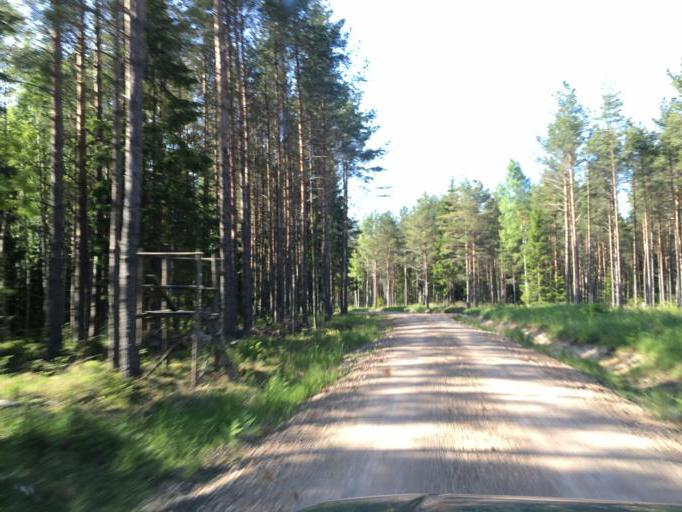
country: LV
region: Dundaga
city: Dundaga
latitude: 57.6104
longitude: 22.5137
